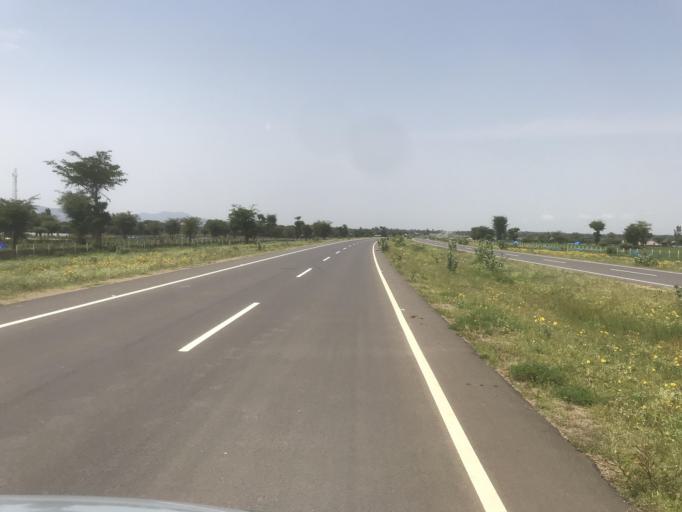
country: ET
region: Oromiya
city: Mojo
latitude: 8.3912
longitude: 39.0101
